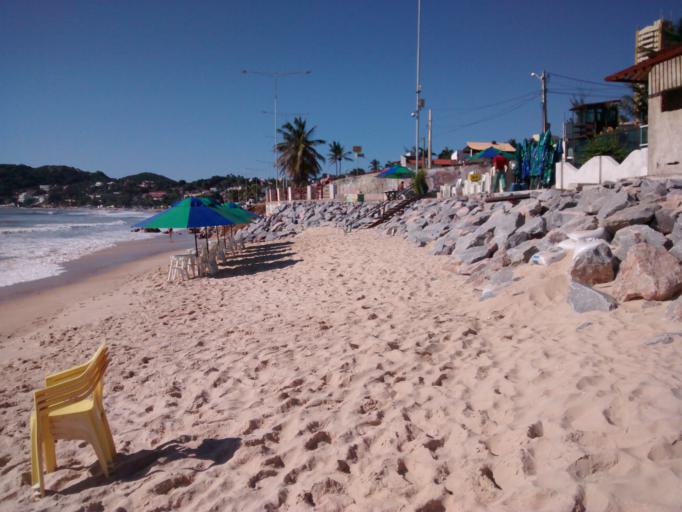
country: BR
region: Rio Grande do Norte
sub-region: Natal
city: Natal
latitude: -5.8781
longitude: -35.1740
